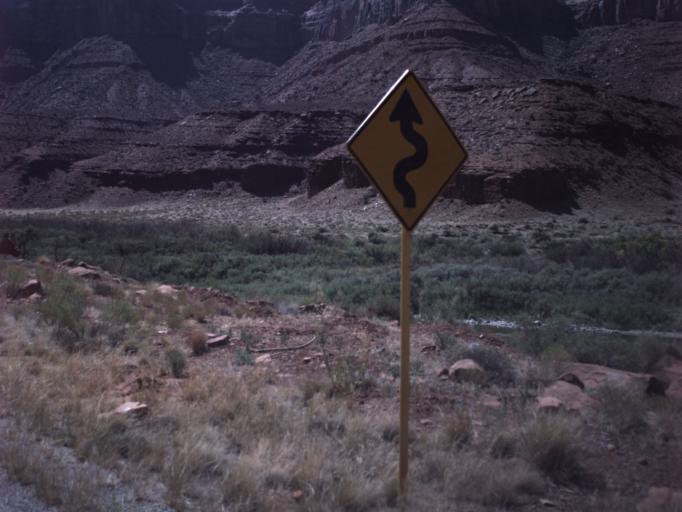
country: US
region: Utah
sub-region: Grand County
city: Moab
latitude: 38.7828
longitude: -109.3324
